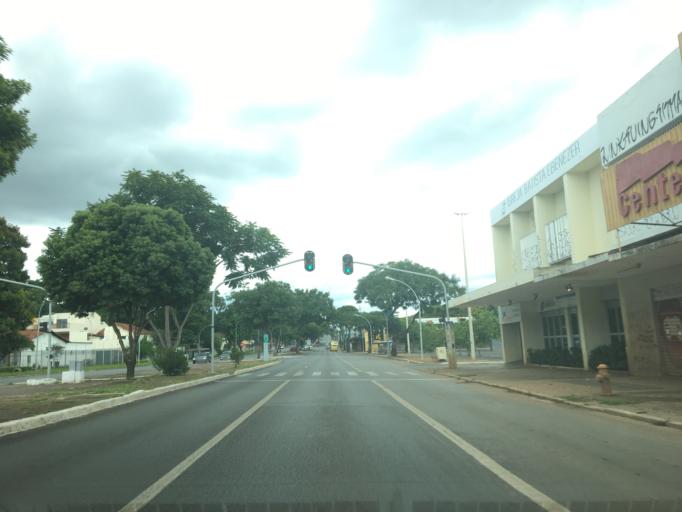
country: BR
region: Federal District
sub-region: Brasilia
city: Brasilia
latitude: -15.8202
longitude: -47.9170
